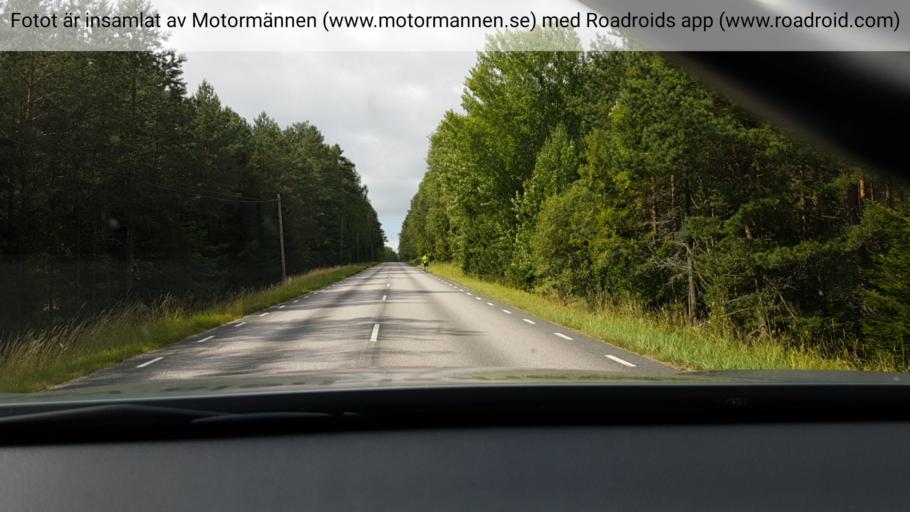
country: SE
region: Stockholm
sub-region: Norrtalje Kommun
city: Rimbo
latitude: 59.7075
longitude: 18.4194
